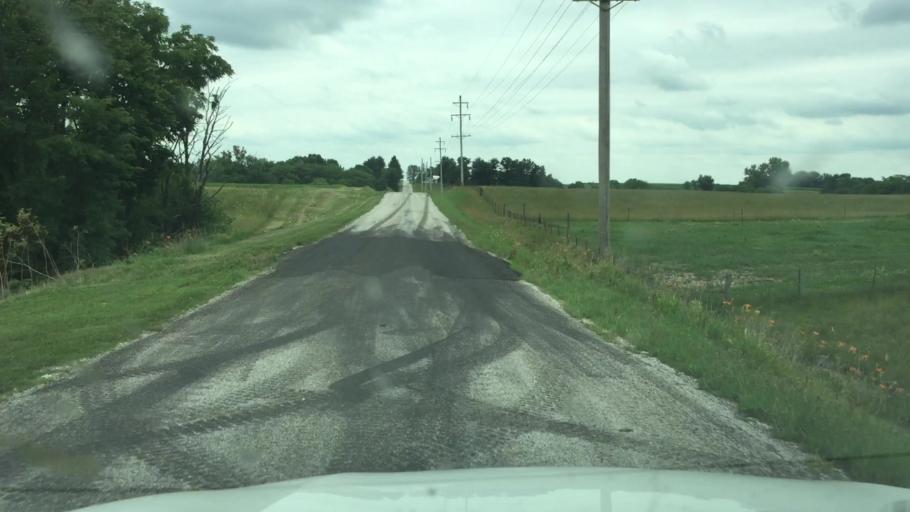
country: US
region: Illinois
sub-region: Hancock County
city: Carthage
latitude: 40.3299
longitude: -91.0825
